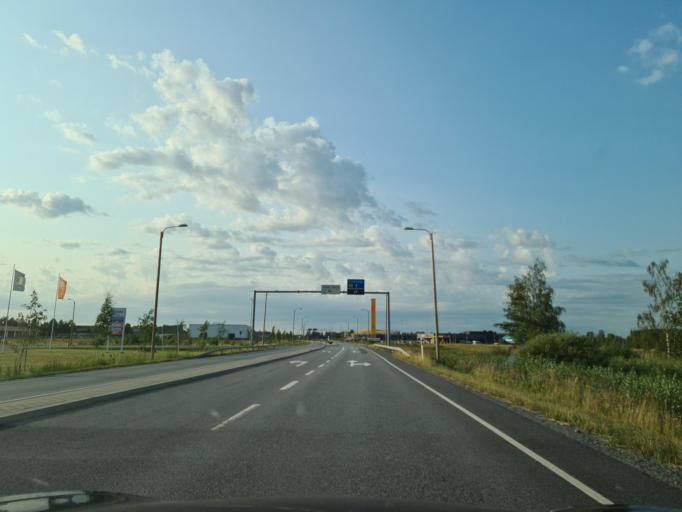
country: FI
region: Southern Ostrobothnia
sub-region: Seinaejoki
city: Kauhava
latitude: 63.0868
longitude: 23.0592
